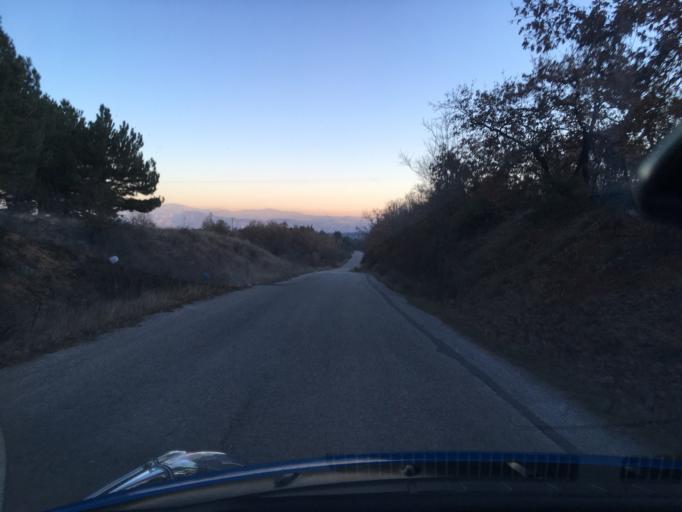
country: GR
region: West Macedonia
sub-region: Nomos Kozanis
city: Kozani
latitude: 40.2649
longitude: 21.7466
